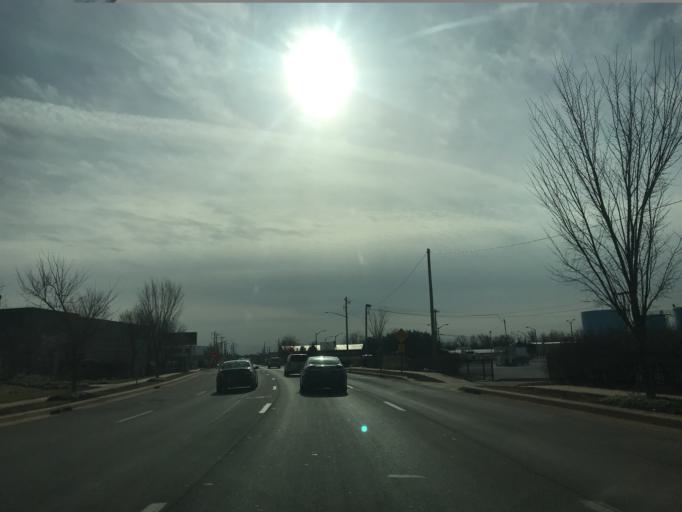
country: US
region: Delaware
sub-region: New Castle County
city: Wilmington
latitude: 39.7329
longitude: -75.5563
